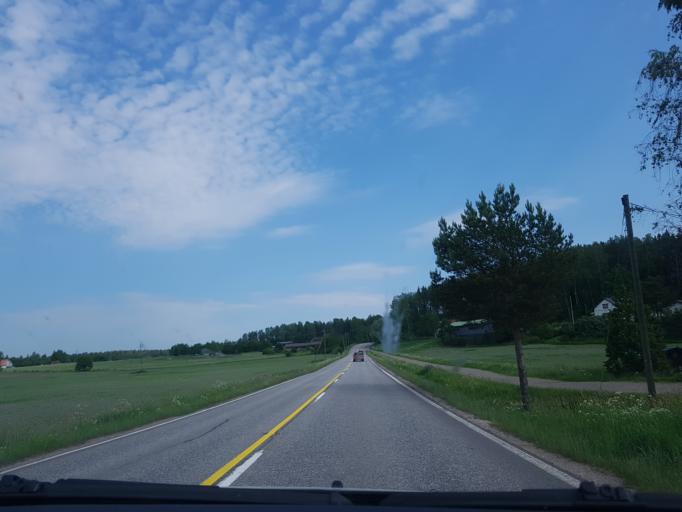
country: FI
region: Uusimaa
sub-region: Helsinki
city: Vihti
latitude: 60.3198
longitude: 24.4034
